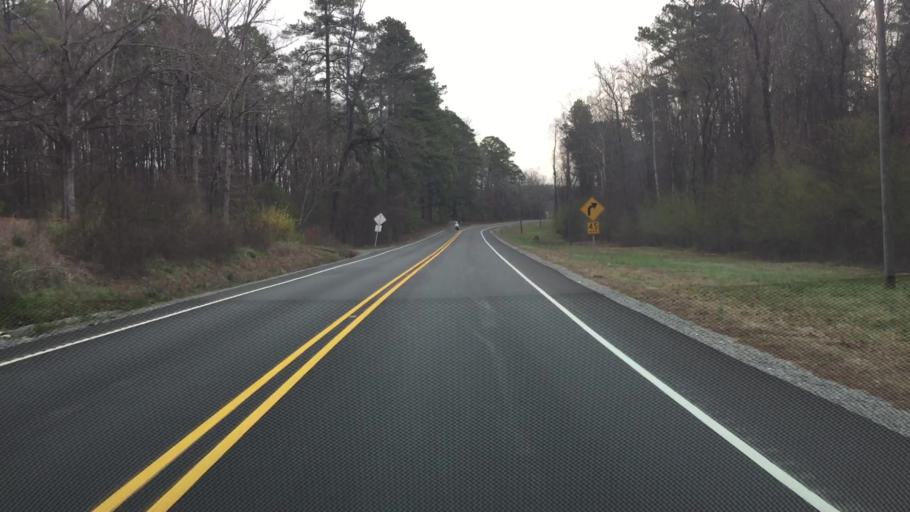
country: US
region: Arkansas
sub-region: Saline County
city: Haskell
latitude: 34.6158
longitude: -92.7873
